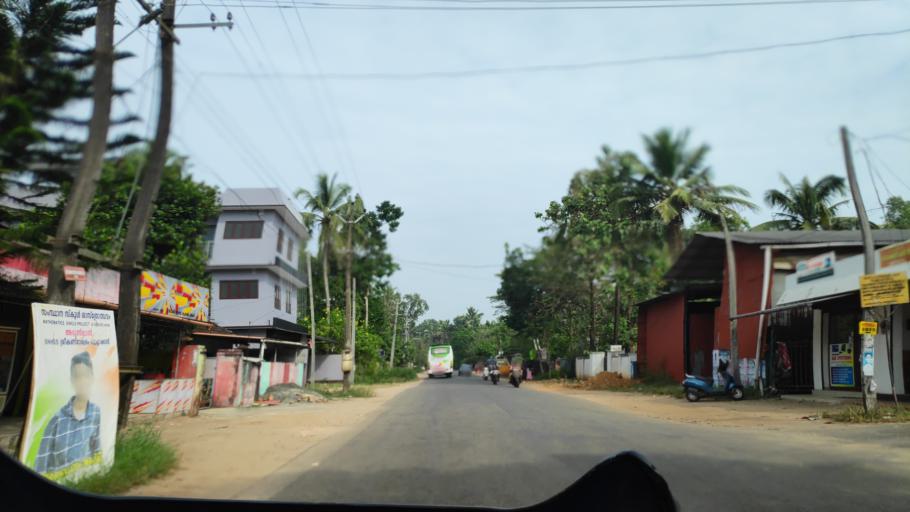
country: IN
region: Kerala
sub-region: Alappuzha
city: Kutiatodu
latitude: 9.8098
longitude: 76.3528
